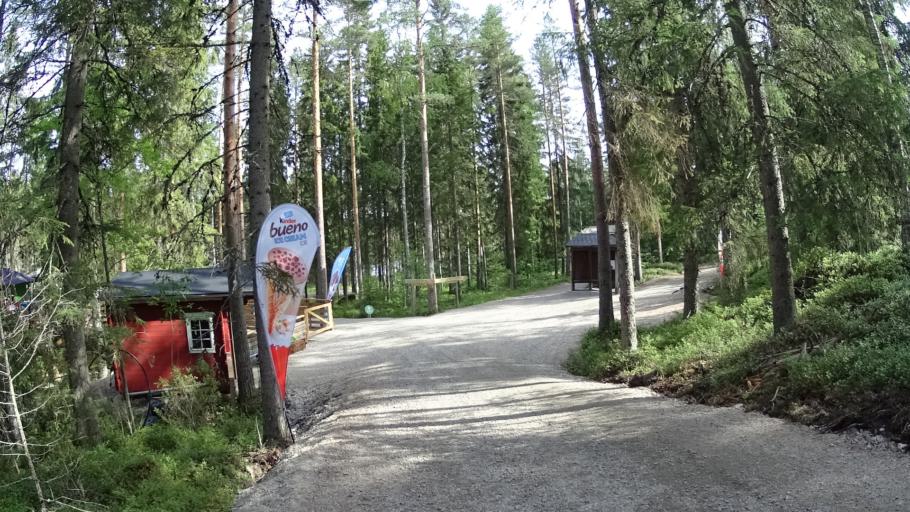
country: FI
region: Southern Ostrobothnia
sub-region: Kuusiokunnat
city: AEhtaeri
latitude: 62.5383
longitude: 24.1837
